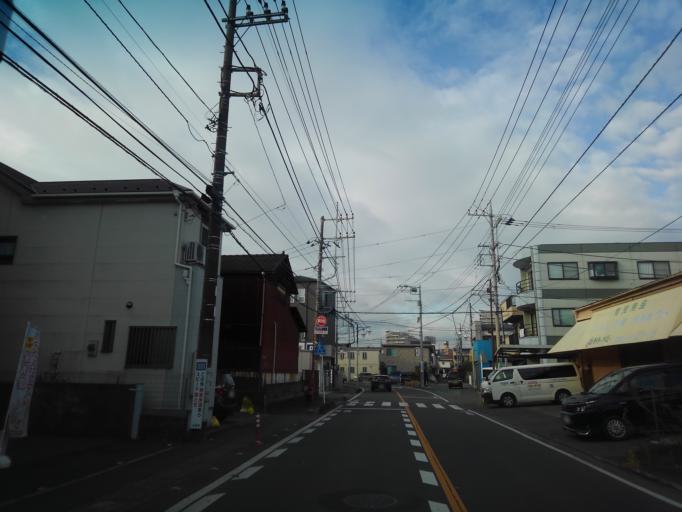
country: JP
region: Kanagawa
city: Minami-rinkan
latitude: 35.5102
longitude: 139.4500
